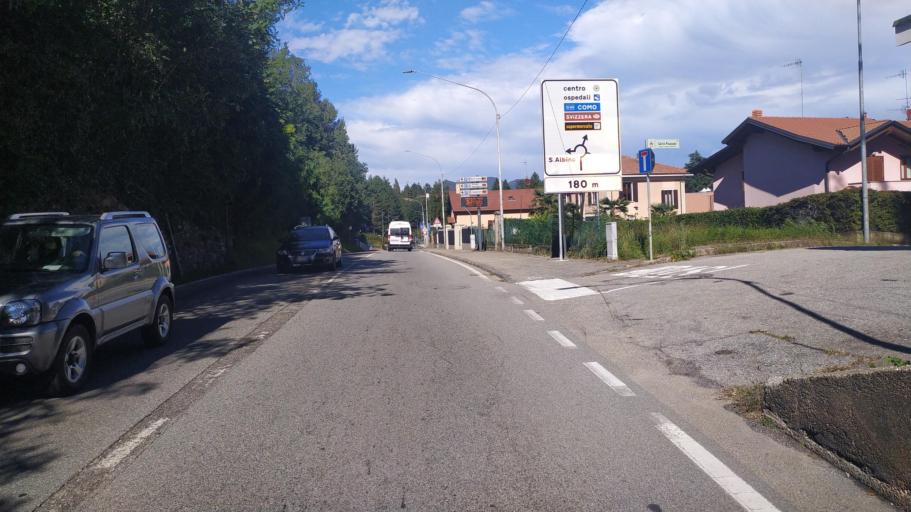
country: IT
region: Lombardy
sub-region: Provincia di Varese
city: Gazzada Schianno
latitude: 45.7986
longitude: 8.8336
